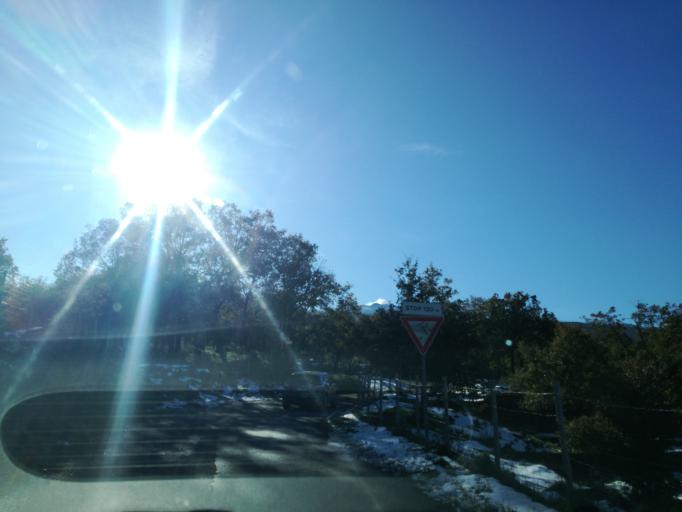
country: IT
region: Sicily
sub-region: Catania
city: Randazzo
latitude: 37.8569
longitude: 14.9840
